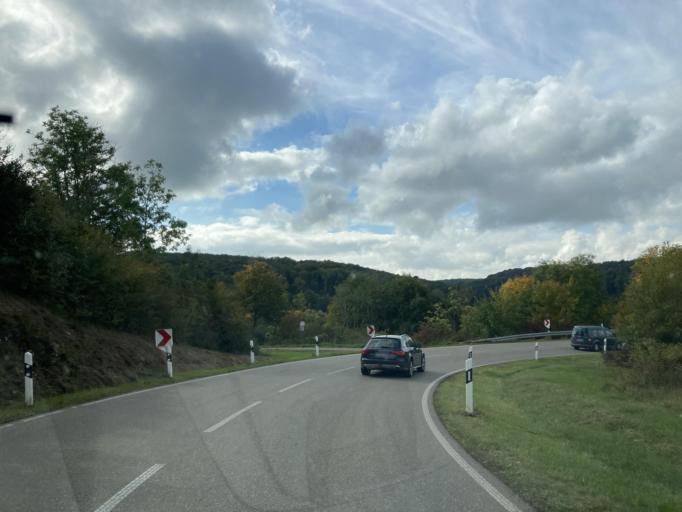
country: DE
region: Baden-Wuerttemberg
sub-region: Regierungsbezirk Stuttgart
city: Hohenstadt
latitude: 48.5456
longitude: 9.6514
